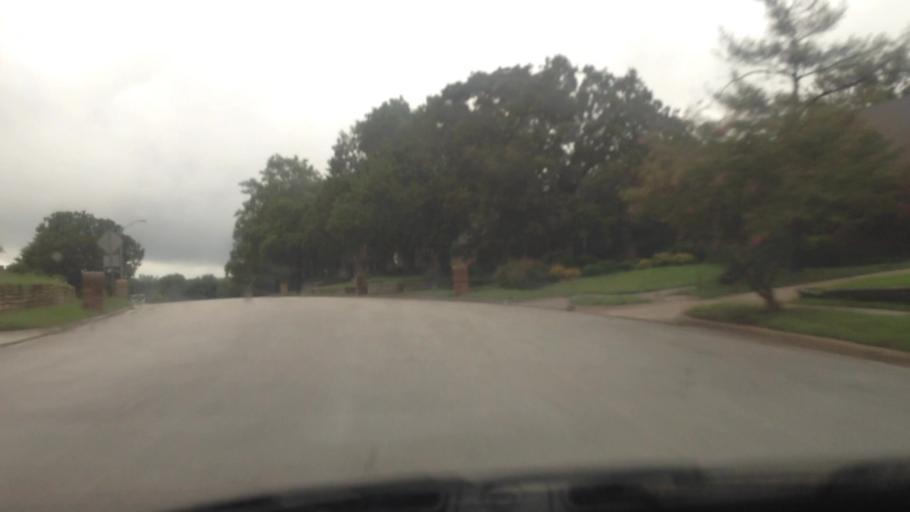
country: US
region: Texas
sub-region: Tarrant County
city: Colleyville
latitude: 32.8759
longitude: -97.1792
